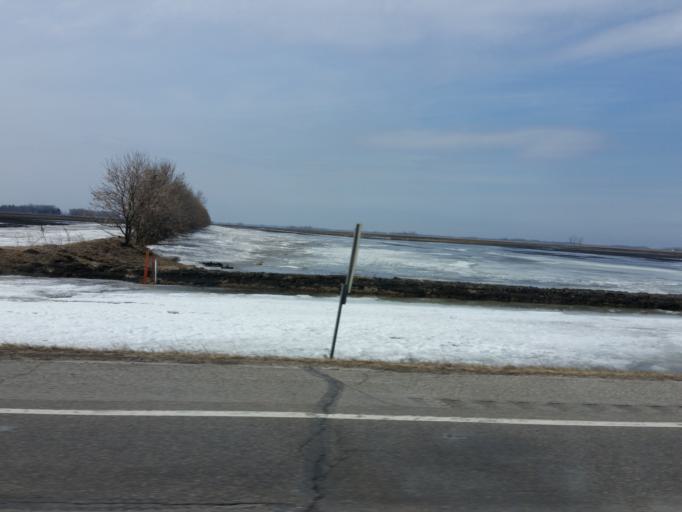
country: US
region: North Dakota
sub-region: Walsh County
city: Grafton
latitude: 48.3469
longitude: -97.4051
